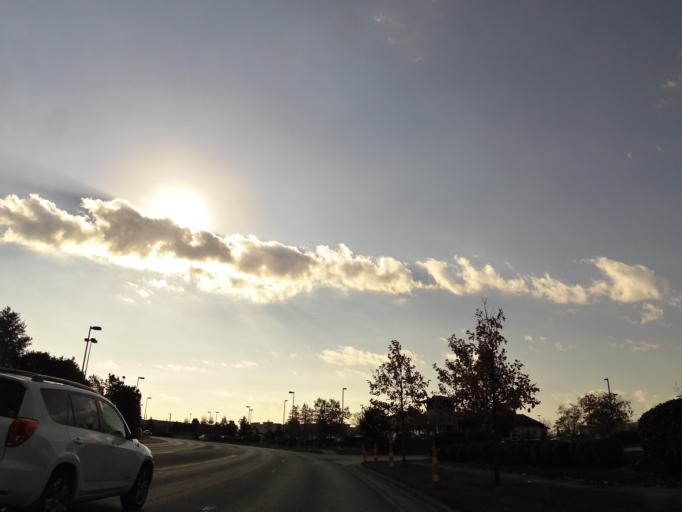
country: US
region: Kentucky
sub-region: Fayette County
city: Lexington-Fayette
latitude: 38.0232
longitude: -84.4231
